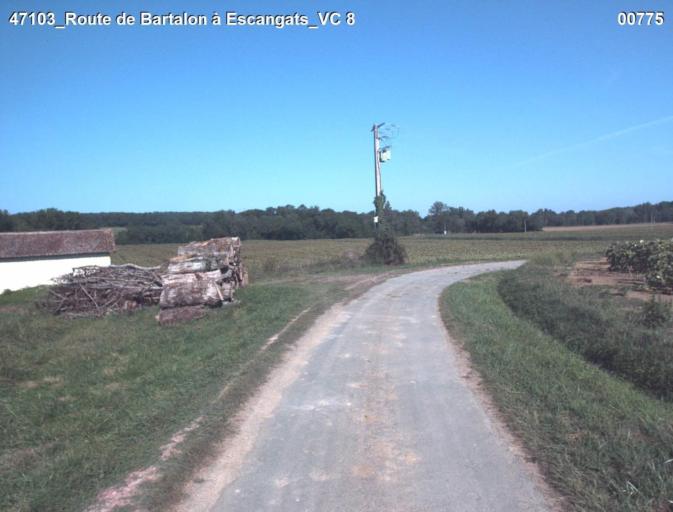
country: FR
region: Aquitaine
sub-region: Departement du Lot-et-Garonne
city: Nerac
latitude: 44.0880
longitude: 0.3144
